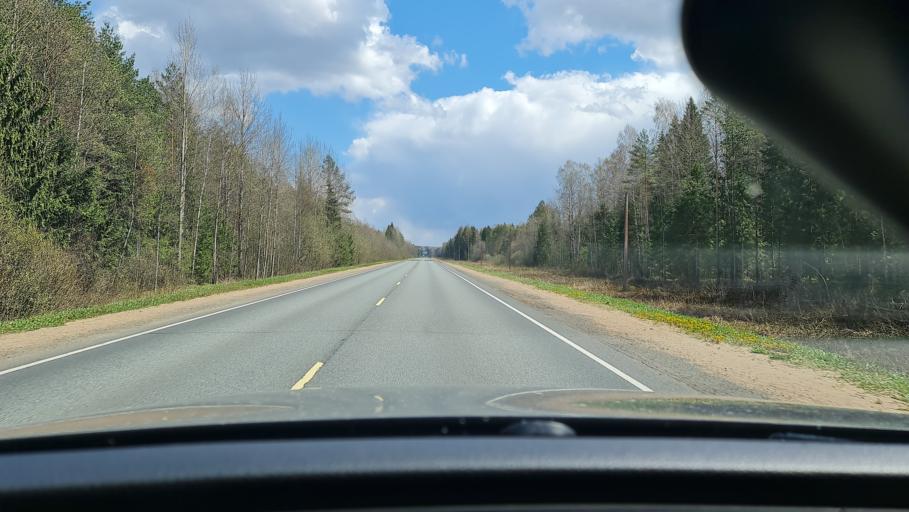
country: RU
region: Tverskaya
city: Zapadnaya Dvina
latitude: 56.3051
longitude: 32.2013
